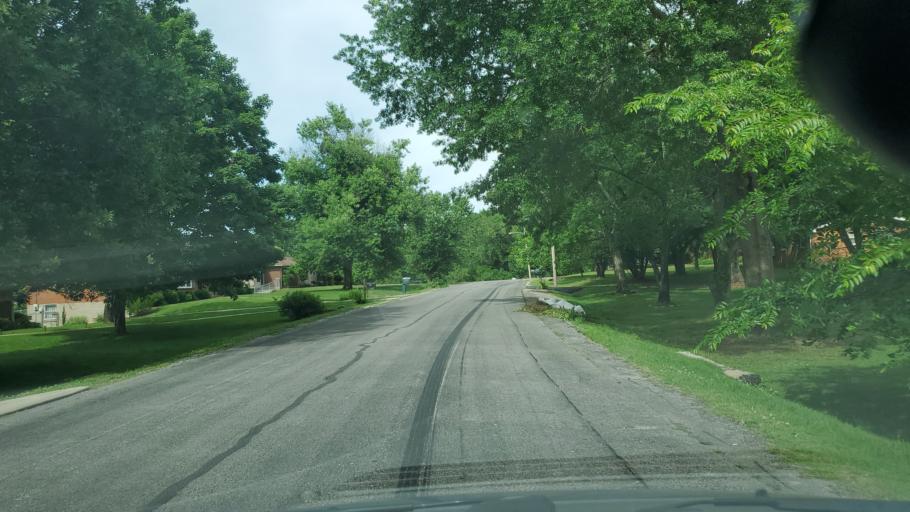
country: US
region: Tennessee
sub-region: Davidson County
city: Lakewood
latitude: 36.2050
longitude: -86.6827
